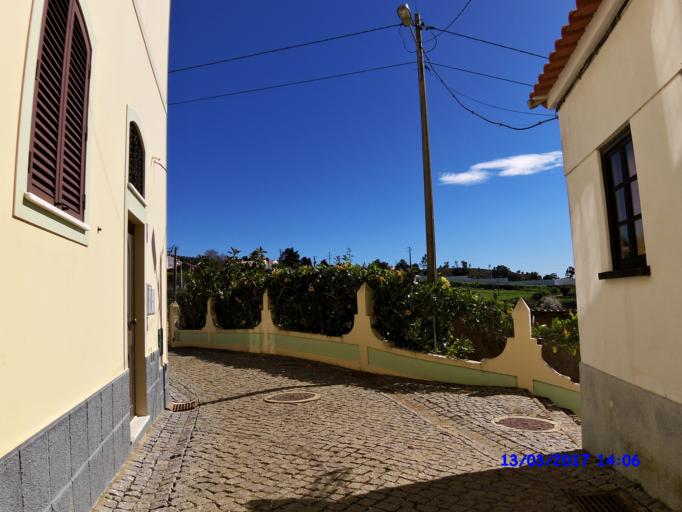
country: PT
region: Faro
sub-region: Monchique
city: Monchique
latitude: 37.3111
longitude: -8.6692
